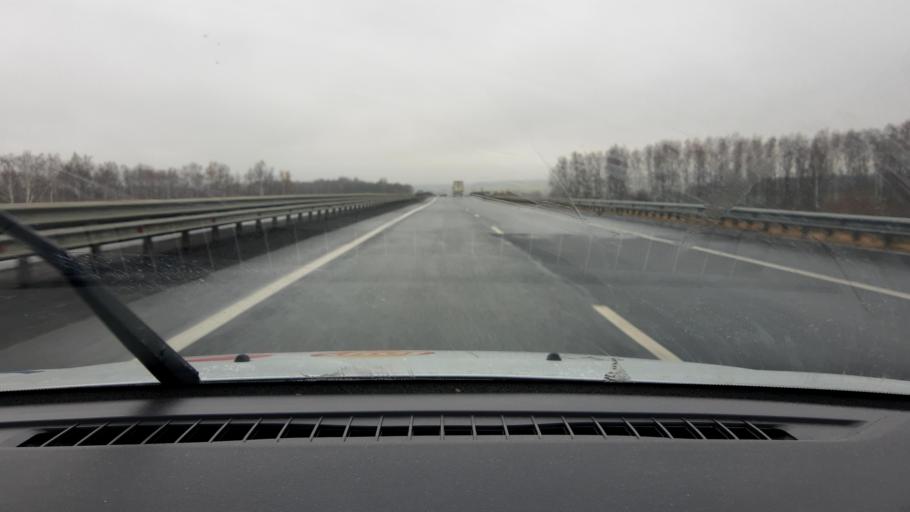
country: RU
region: Nizjnij Novgorod
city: Burevestnik
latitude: 56.1337
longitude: 43.7740
